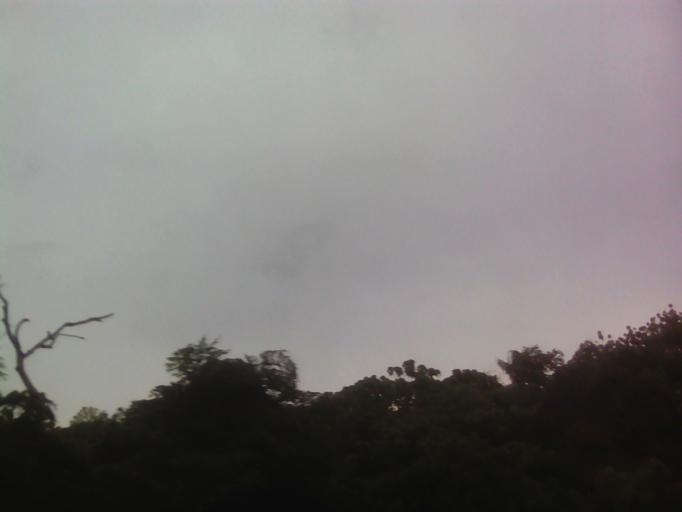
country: MY
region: Penang
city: Perai
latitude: 5.3981
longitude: 100.4129
